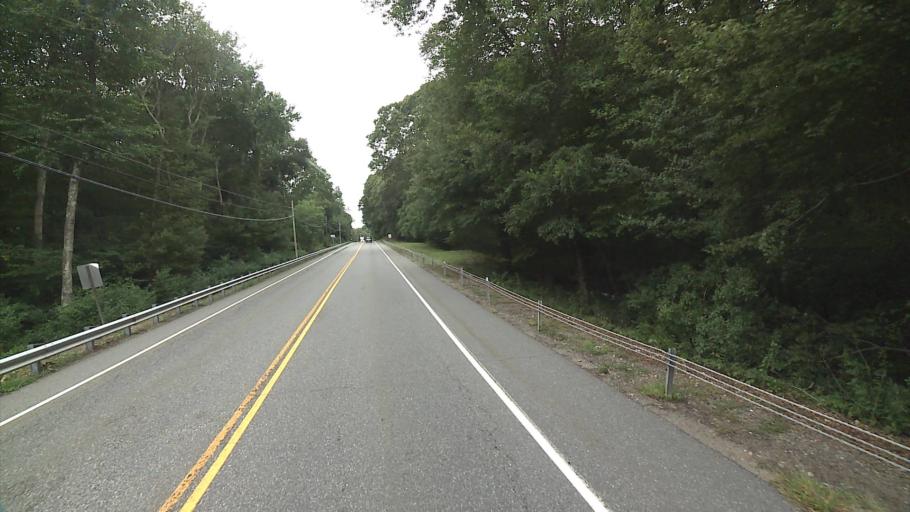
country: US
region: Connecticut
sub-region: Middlesex County
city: Old Saybrook Center
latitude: 41.2865
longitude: -72.3020
